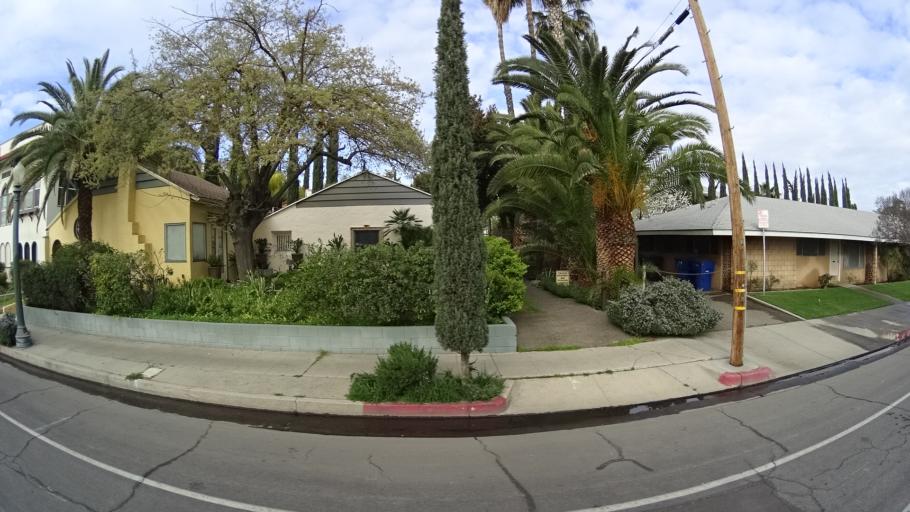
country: US
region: California
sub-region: Fresno County
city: Fresno
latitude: 36.7618
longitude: -119.8011
